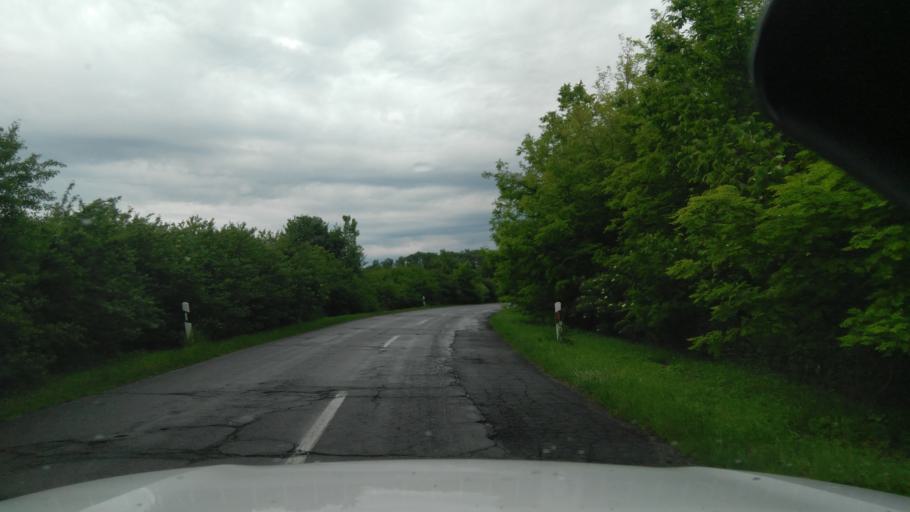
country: HU
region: Bekes
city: Bekescsaba
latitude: 46.6841
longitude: 21.1663
